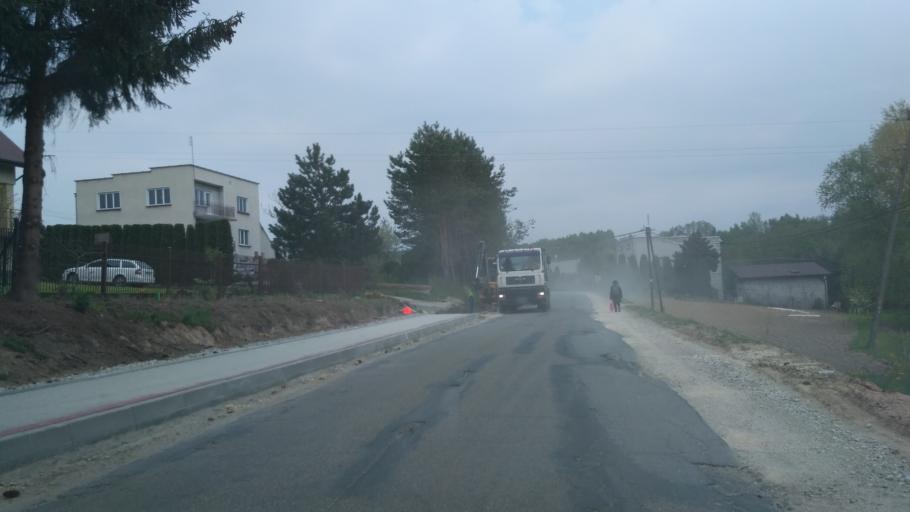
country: PL
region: Lesser Poland Voivodeship
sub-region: Powiat tarnowski
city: Skrzyszow
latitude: 49.9789
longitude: 21.0650
